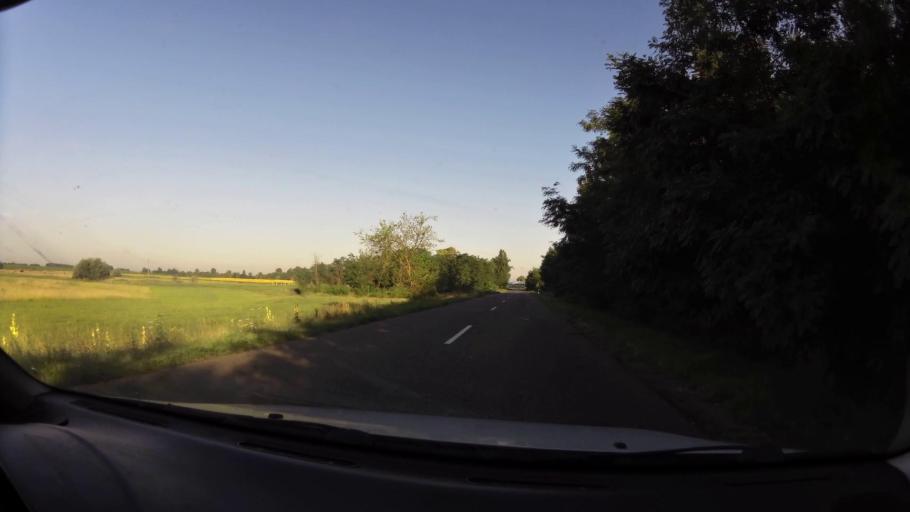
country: HU
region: Pest
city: Tapioszolos
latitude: 47.2821
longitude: 19.8732
